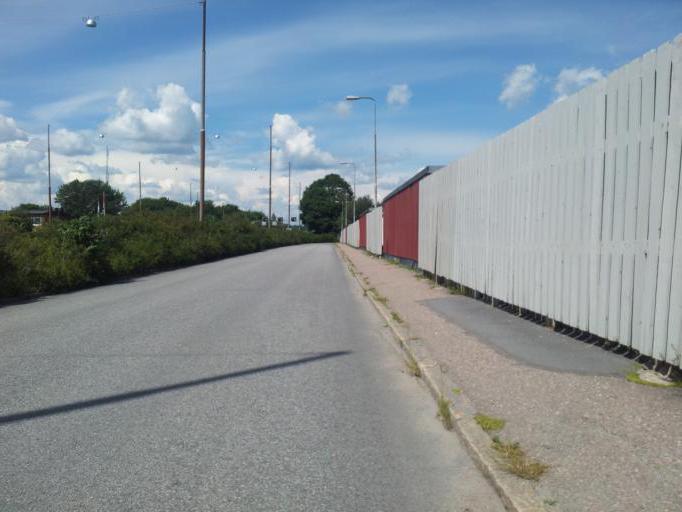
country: SE
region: Uppsala
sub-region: Uppsala Kommun
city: Uppsala
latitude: 59.8713
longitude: 17.6536
